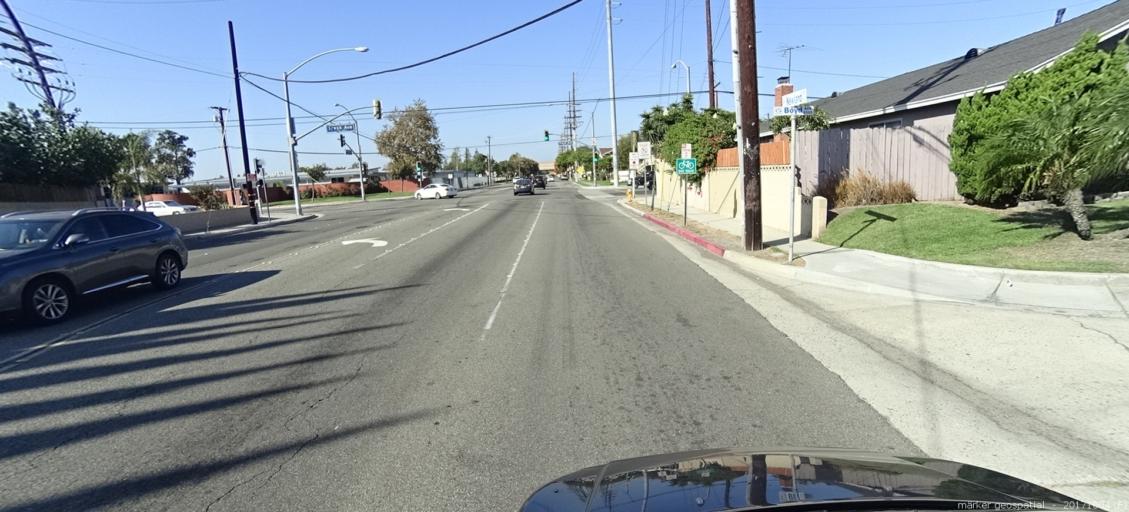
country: US
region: California
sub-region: Orange County
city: Midway City
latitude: 33.7661
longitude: -117.9811
